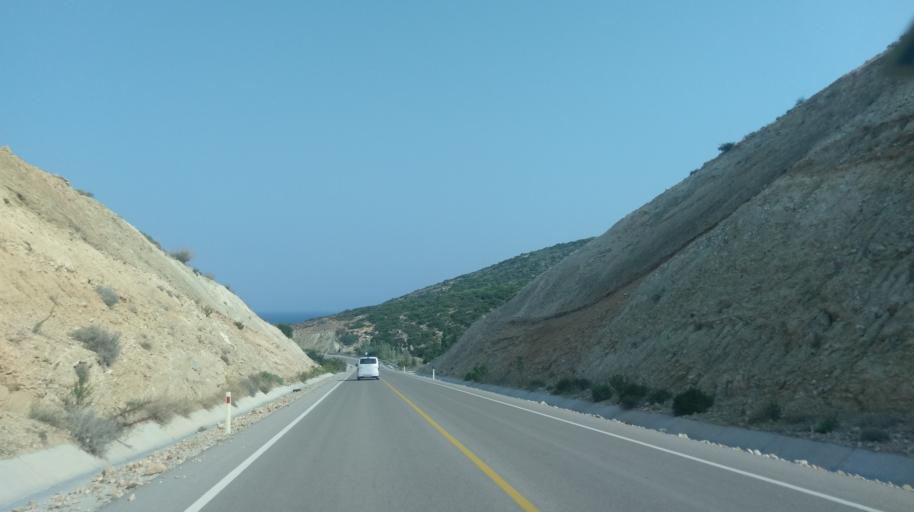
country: CY
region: Ammochostos
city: Leonarisso
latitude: 35.4553
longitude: 34.0081
